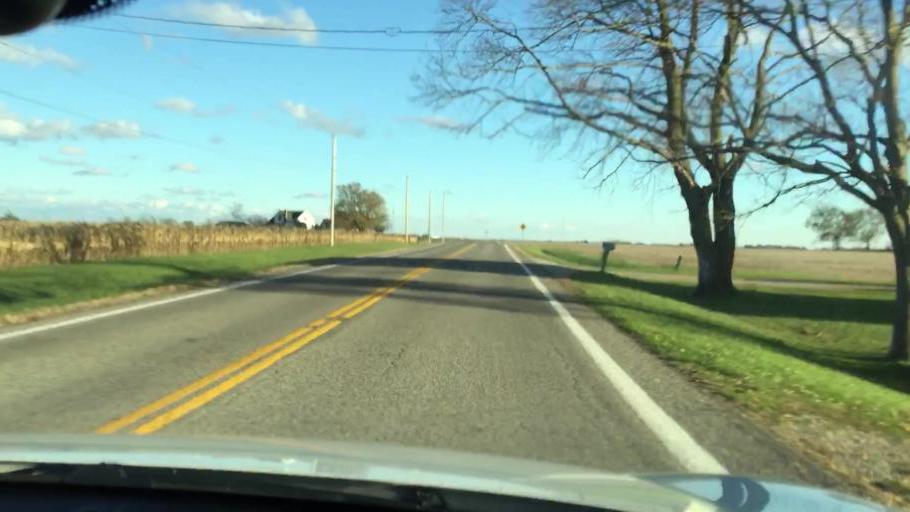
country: US
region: Ohio
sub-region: Champaign County
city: North Lewisburg
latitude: 40.1900
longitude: -83.5212
